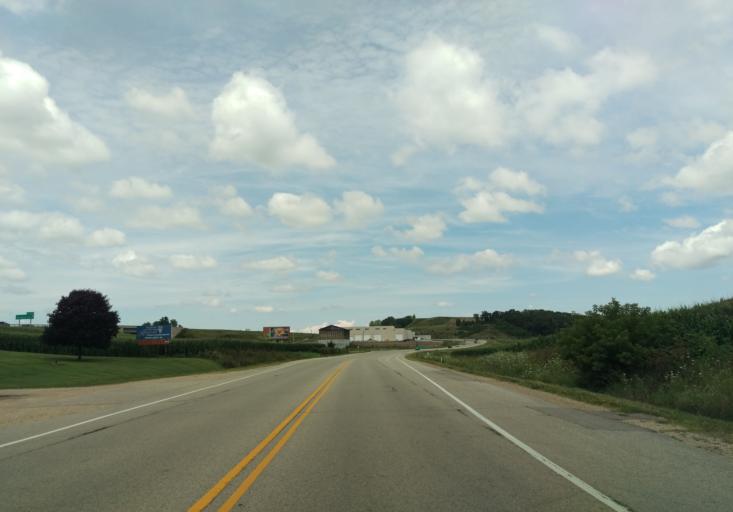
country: US
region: Wisconsin
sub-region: Dane County
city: Middleton
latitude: 43.1188
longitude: -89.5128
